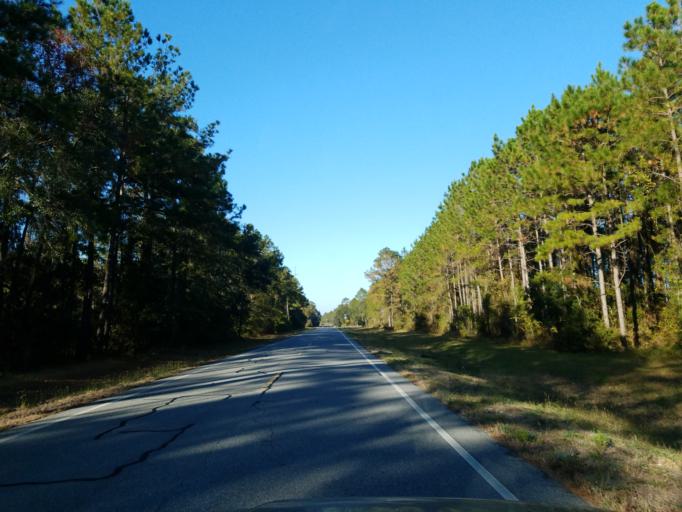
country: US
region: Georgia
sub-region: Echols County
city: Statenville
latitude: 30.6547
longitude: -83.0633
